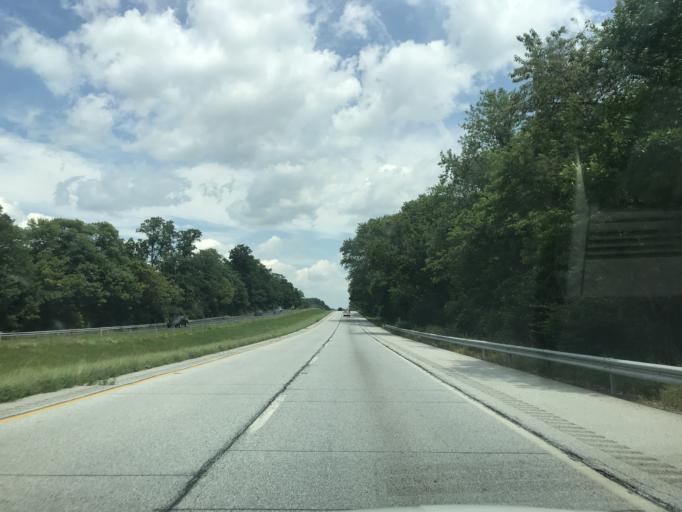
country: US
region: Pennsylvania
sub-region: Chester County
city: Oxford
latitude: 39.7675
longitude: -76.0132
